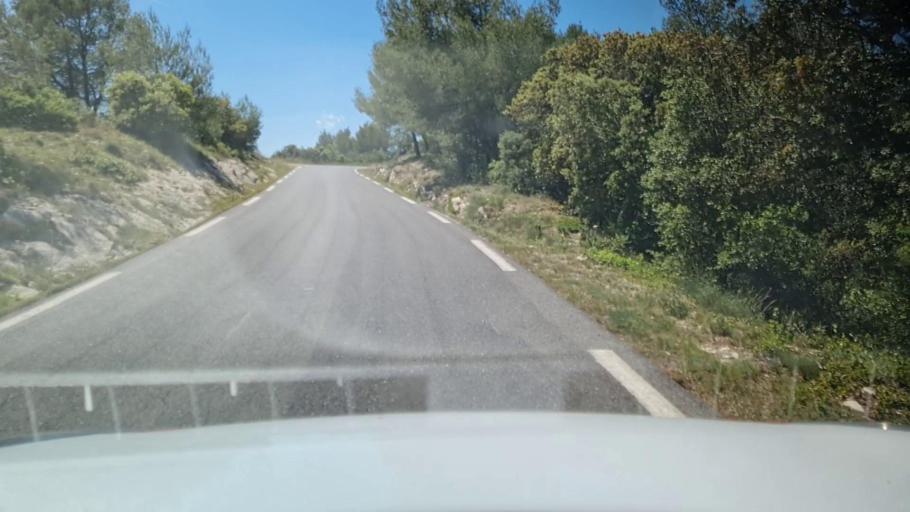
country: FR
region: Languedoc-Roussillon
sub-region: Departement du Gard
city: Clarensac
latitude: 43.8365
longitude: 4.2261
